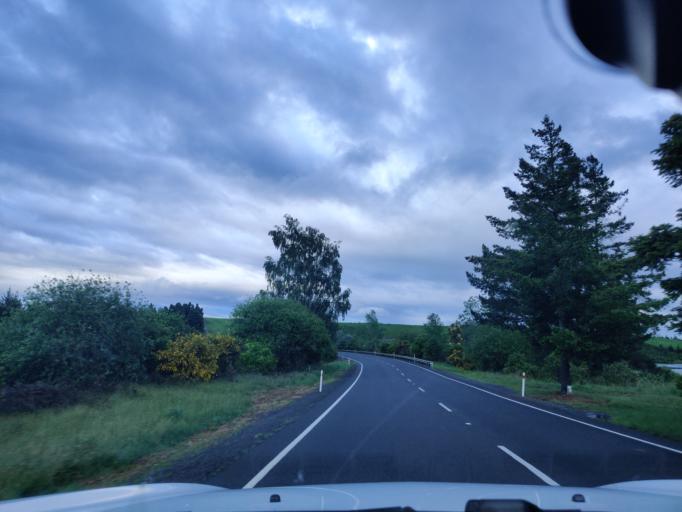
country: NZ
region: Waikato
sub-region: South Waikato District
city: Tokoroa
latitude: -38.3743
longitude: 175.7964
